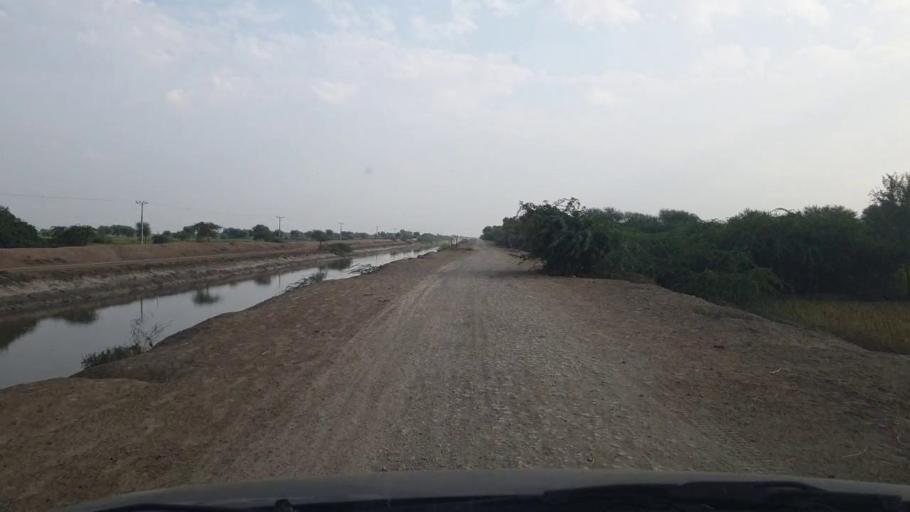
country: PK
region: Sindh
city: Badin
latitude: 24.5226
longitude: 68.6815
